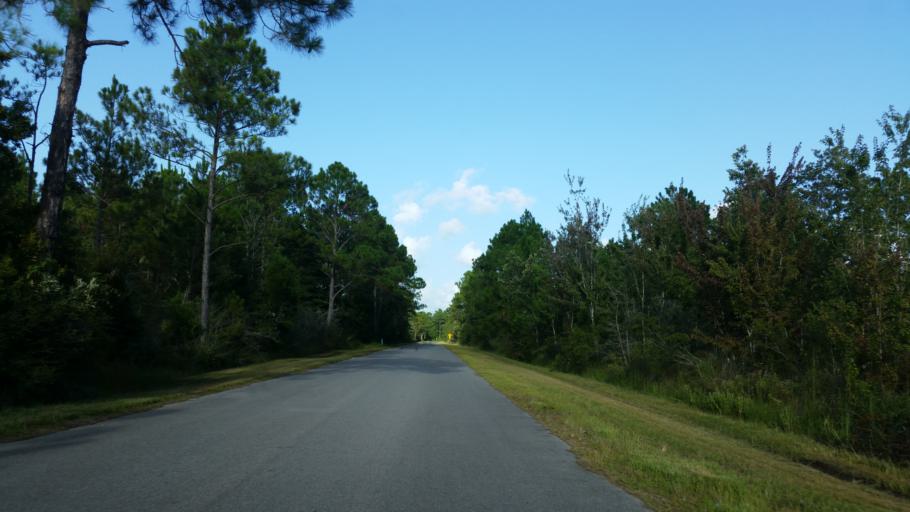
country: US
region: Florida
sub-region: Santa Rosa County
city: Pace
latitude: 30.5346
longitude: -87.1117
